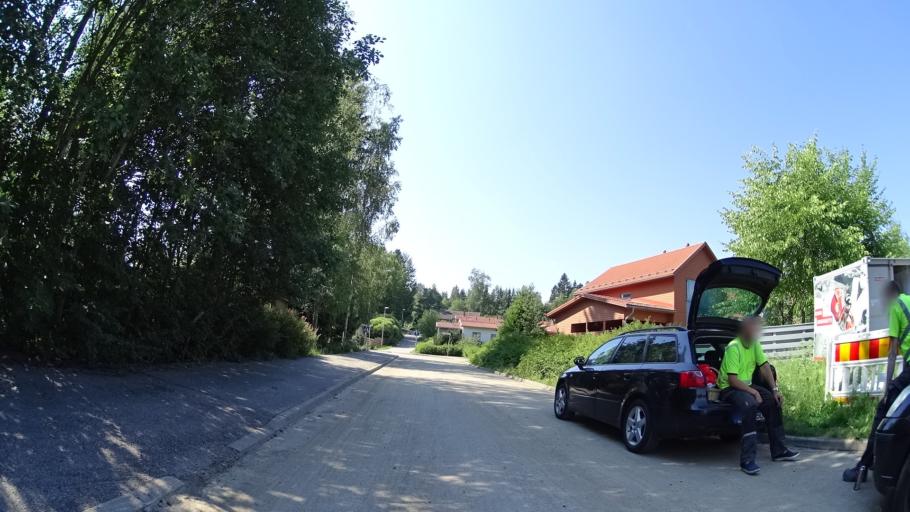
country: FI
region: Uusimaa
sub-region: Helsinki
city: Kerava
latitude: 60.3605
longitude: 25.0733
